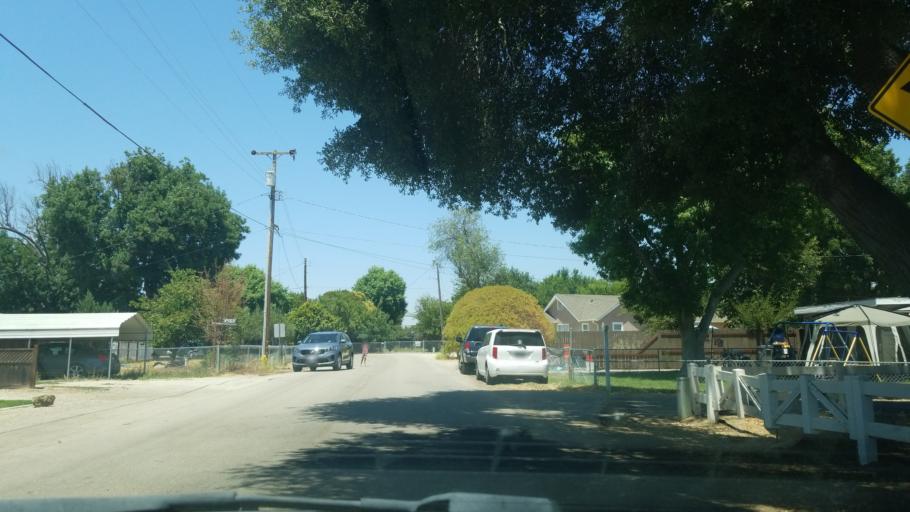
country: US
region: California
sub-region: San Luis Obispo County
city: Atascadero
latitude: 35.5077
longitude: -120.6635
